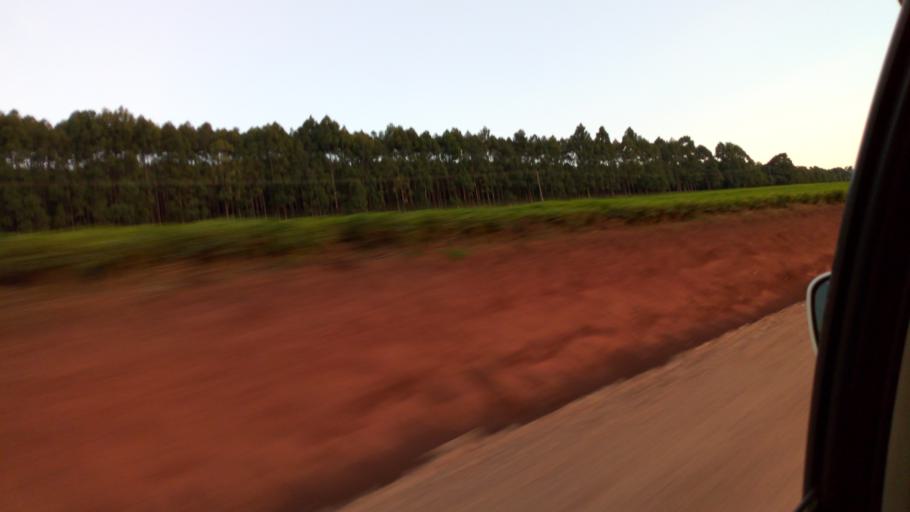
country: KE
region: Nyamira District
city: Nyamira
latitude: -0.5969
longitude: 35.0571
